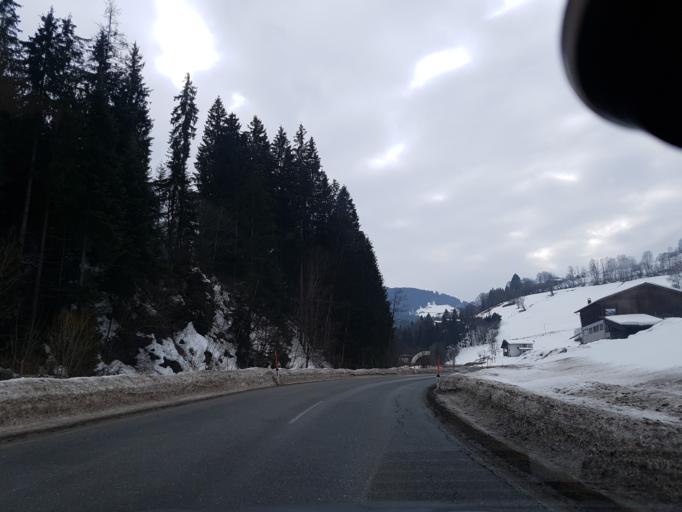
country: AT
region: Tyrol
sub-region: Politischer Bezirk Kufstein
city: Worgl
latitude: 47.4570
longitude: 12.0941
